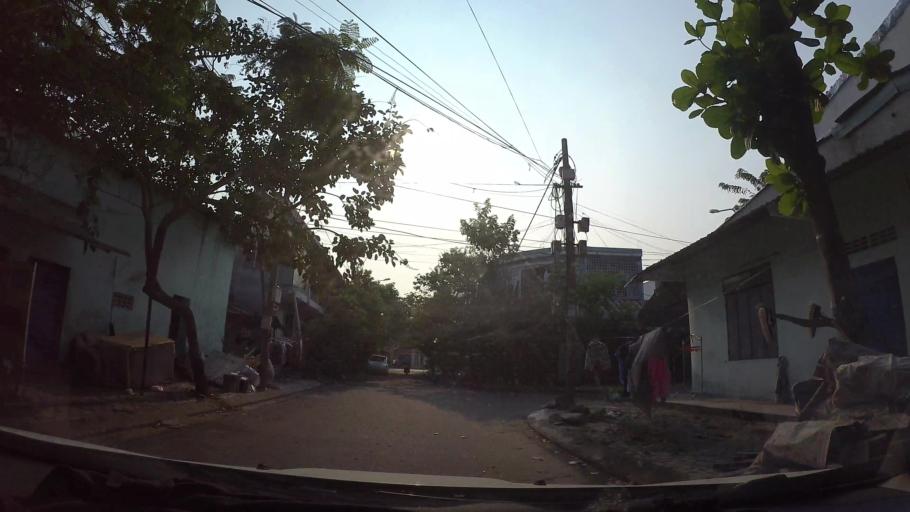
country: VN
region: Da Nang
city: Cam Le
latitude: 16.0217
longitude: 108.2031
